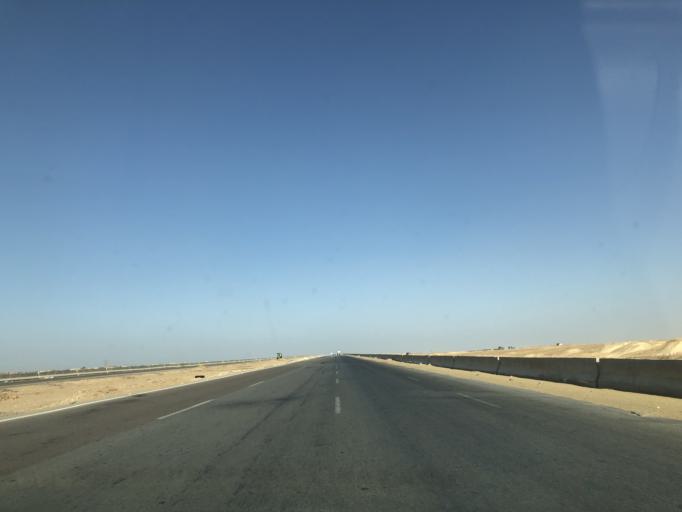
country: EG
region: Muhafazat al Minufiyah
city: Ashmun
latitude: 30.0675
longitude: 30.8587
